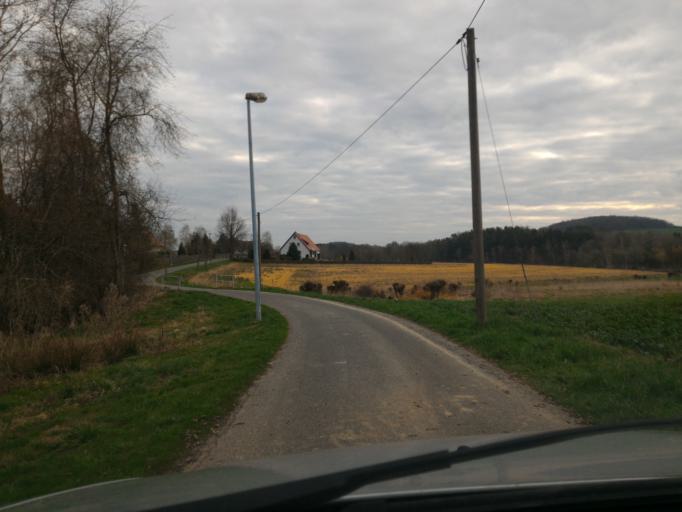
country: DE
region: Saxony
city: Leutersdorf
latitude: 50.9620
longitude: 14.6653
